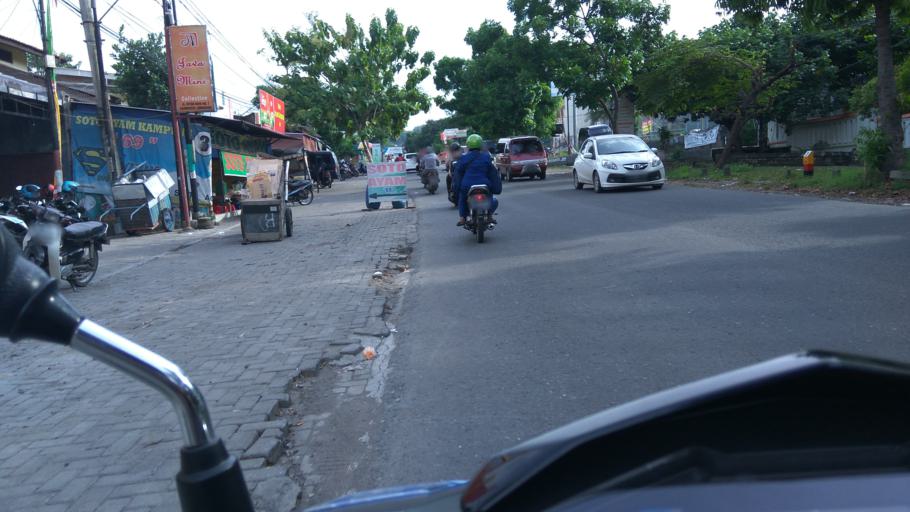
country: ID
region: Central Java
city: Semarang
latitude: -7.0312
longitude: 110.4587
